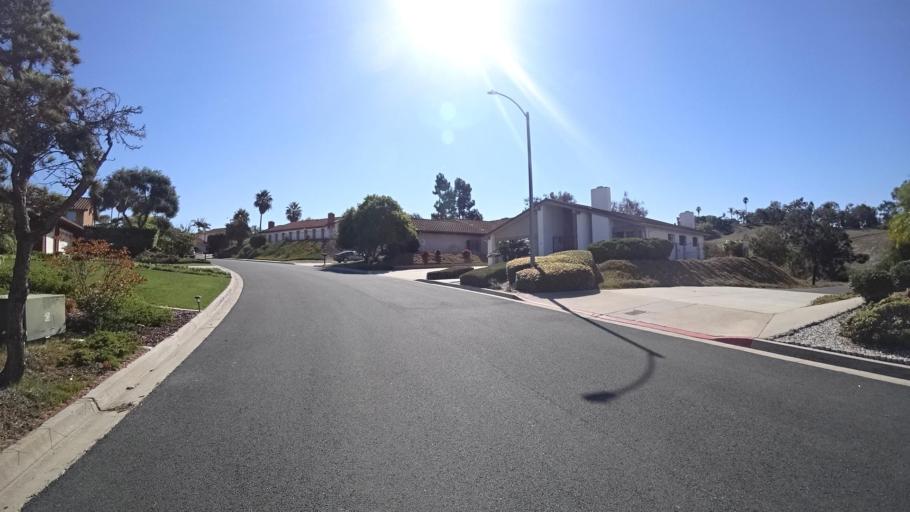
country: US
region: California
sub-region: San Diego County
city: Bonita
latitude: 32.6692
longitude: -117.0133
